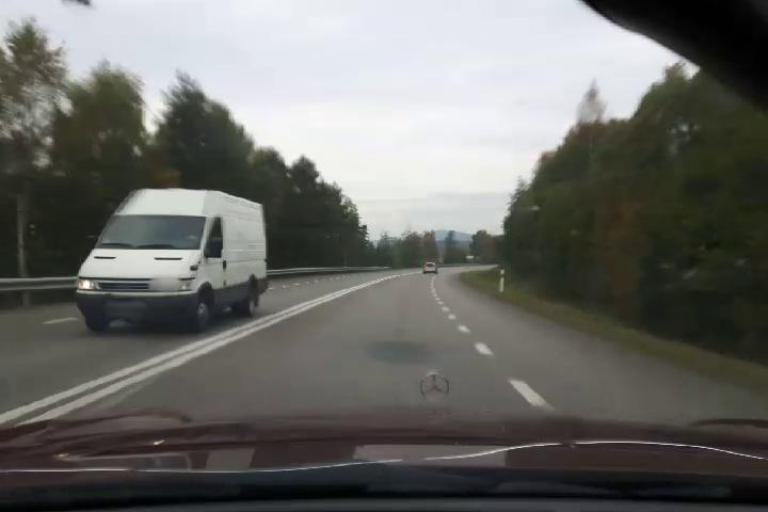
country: SE
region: Vaesternorrland
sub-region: Kramfors Kommun
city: Nordingra
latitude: 63.0093
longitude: 18.2244
